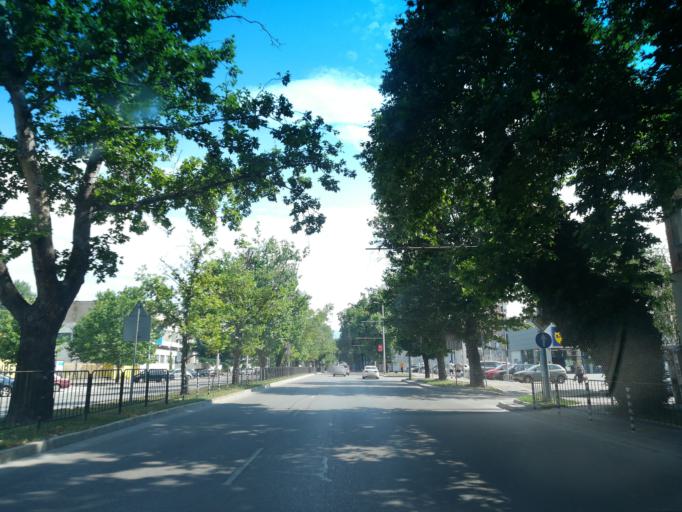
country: BG
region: Plovdiv
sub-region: Obshtina Plovdiv
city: Plovdiv
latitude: 42.1401
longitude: 24.7630
